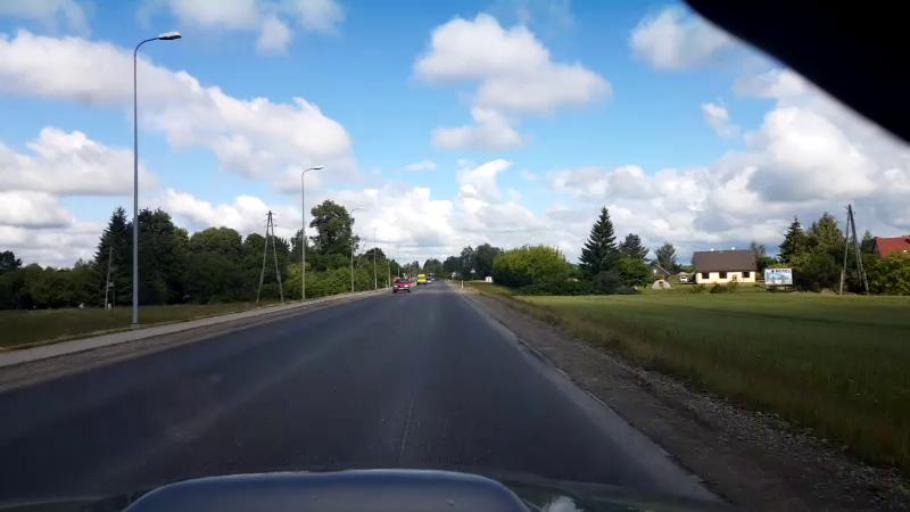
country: LV
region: Bauskas Rajons
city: Bauska
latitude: 56.4015
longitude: 24.2246
